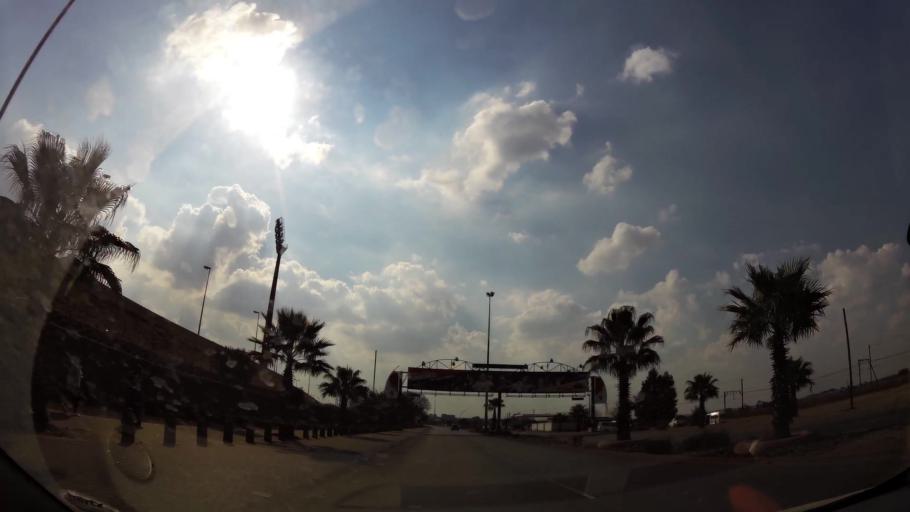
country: ZA
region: Gauteng
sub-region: Ekurhuleni Metropolitan Municipality
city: Germiston
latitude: -26.3043
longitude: 28.1594
